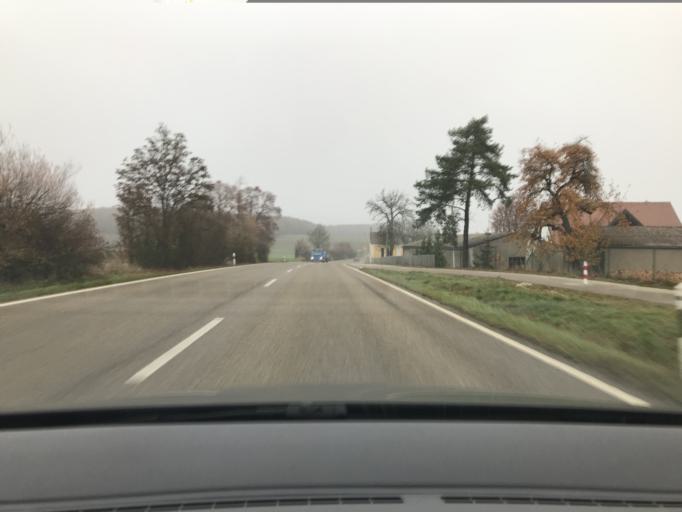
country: DE
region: Bavaria
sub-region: Swabia
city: Marktoffingen
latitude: 48.9413
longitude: 10.4599
